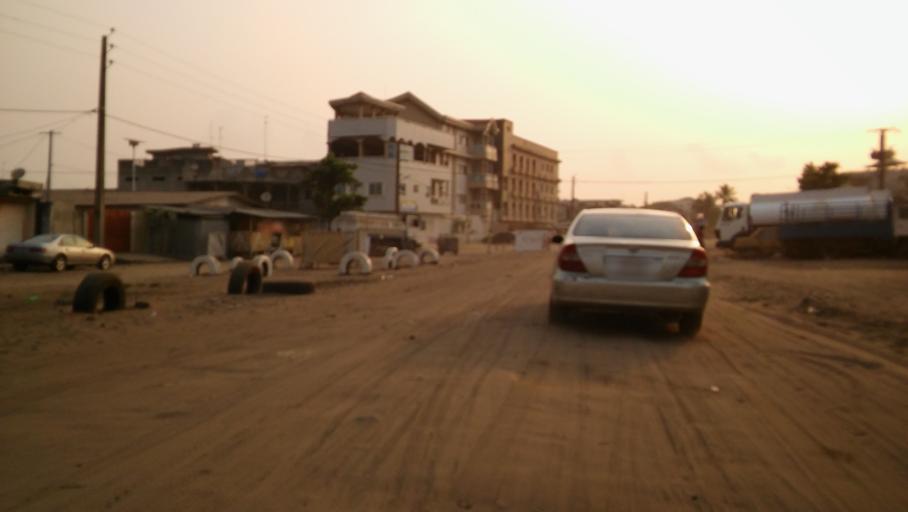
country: BJ
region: Littoral
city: Cotonou
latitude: 6.3908
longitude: 2.3802
